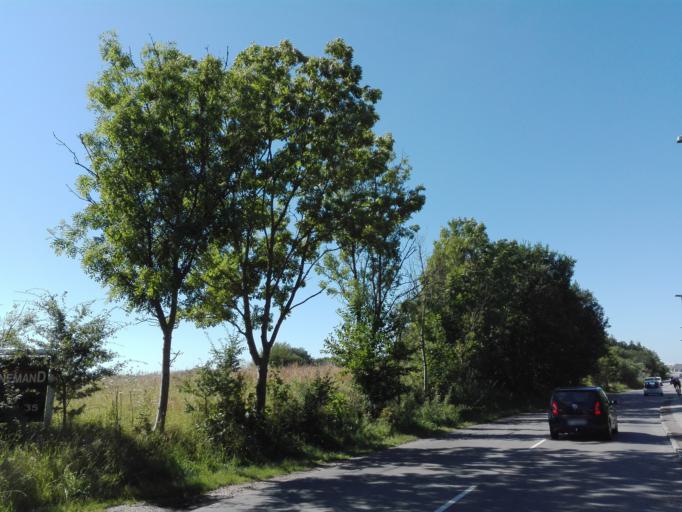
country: DK
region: Central Jutland
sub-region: Arhus Kommune
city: Tranbjerg
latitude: 56.1050
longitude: 10.1388
